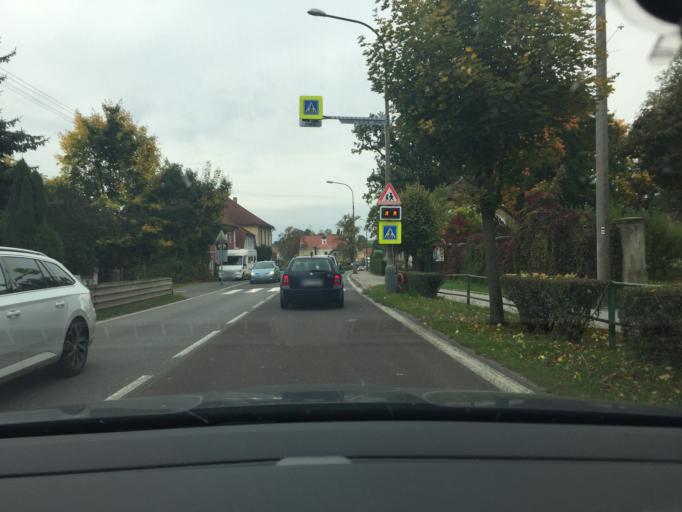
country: CZ
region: Jihocesky
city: Cimelice
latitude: 49.4686
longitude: 14.0698
